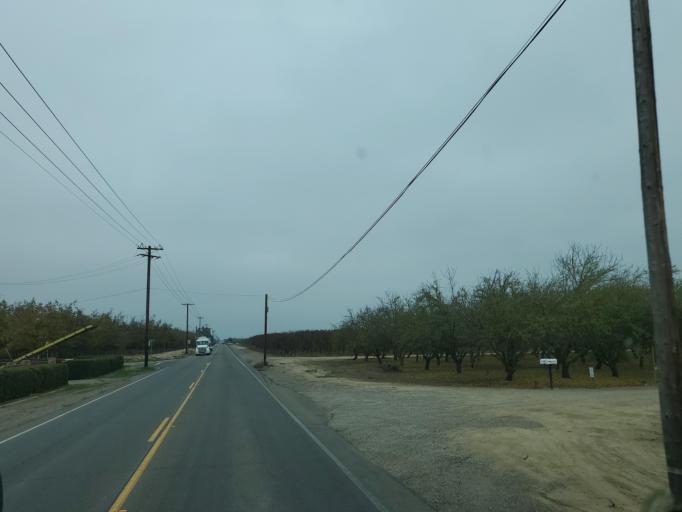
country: US
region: California
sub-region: Stanislaus County
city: Keyes
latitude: 37.5512
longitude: -120.8708
